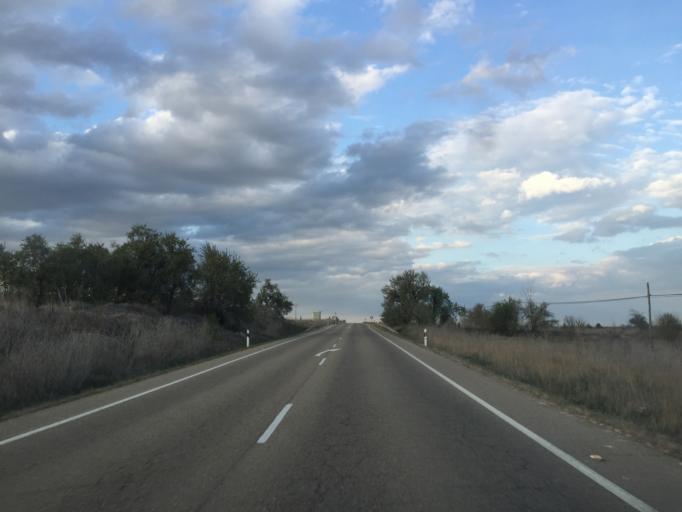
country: ES
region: Castille and Leon
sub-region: Provincia de Palencia
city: Soto de Cerrato
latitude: 41.9531
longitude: -4.4573
